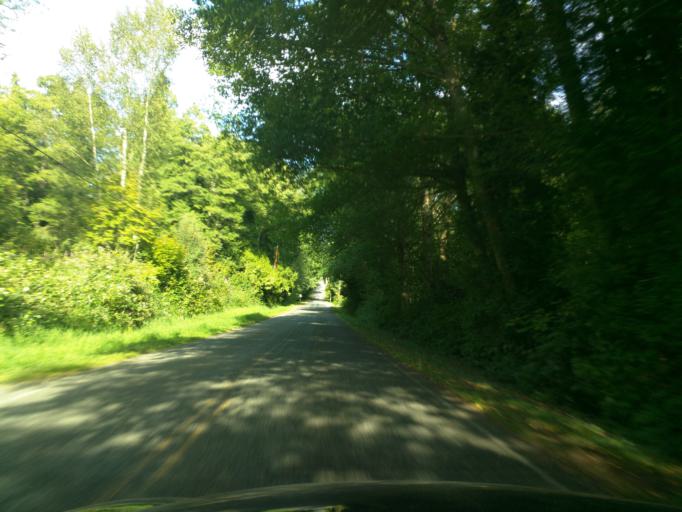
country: US
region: Washington
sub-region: Whatcom County
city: Blaine
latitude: 48.9939
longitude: -122.6999
